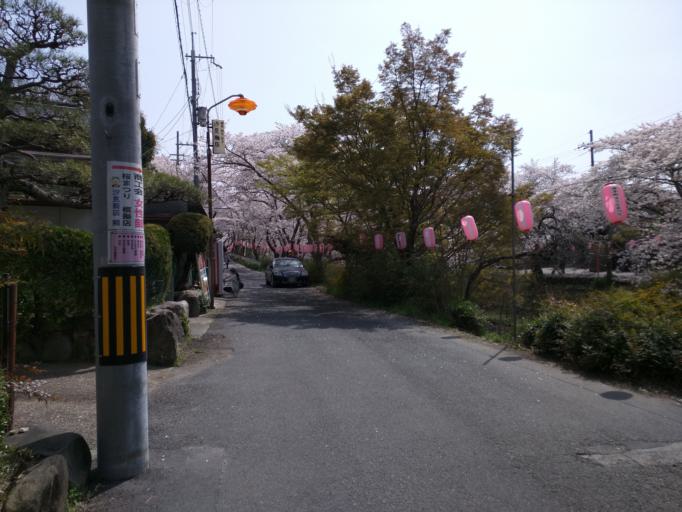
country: JP
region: Kyoto
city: Tanabe
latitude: 34.7985
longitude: 135.8101
